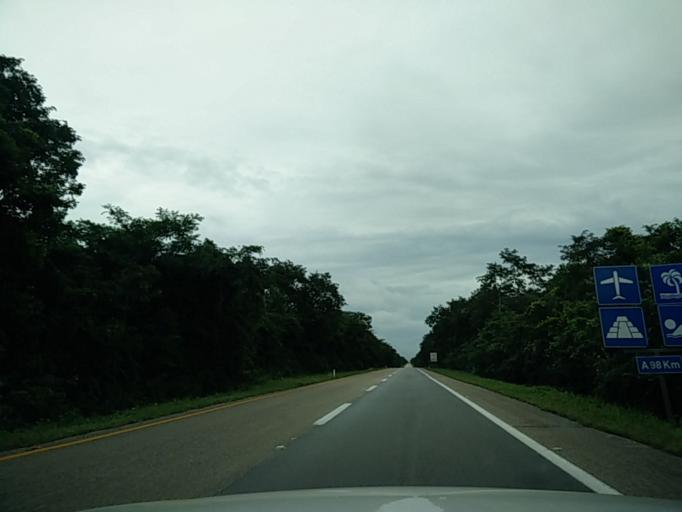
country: MX
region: Quintana Roo
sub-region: Lazaro Cardenas
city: Ignacio Zaragoza
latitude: 20.8895
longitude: -87.5355
